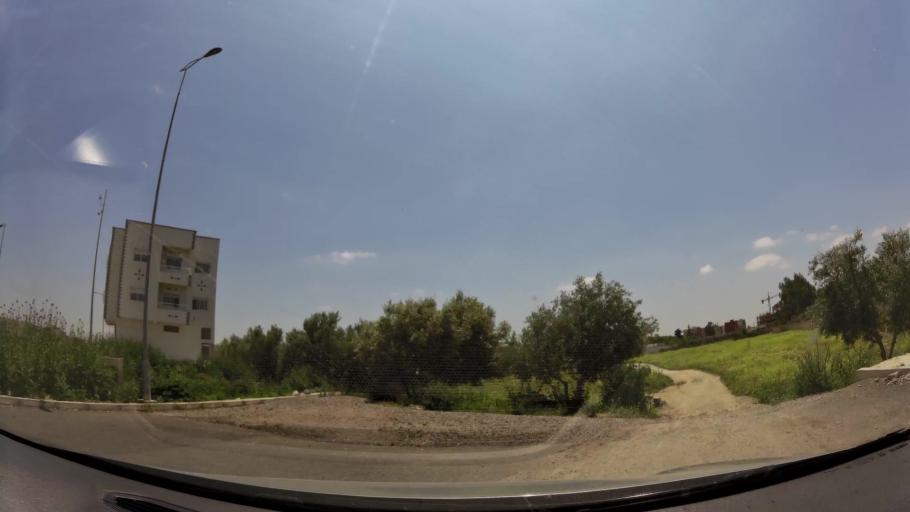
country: MA
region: Fes-Boulemane
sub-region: Fes
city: Fes
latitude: 34.0273
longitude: -5.0535
